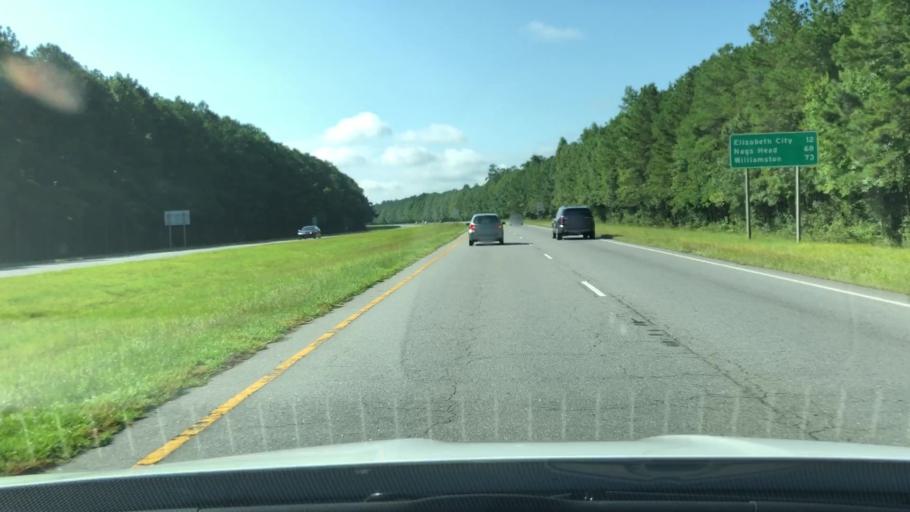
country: US
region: North Carolina
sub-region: Pasquotank County
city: Elizabeth City
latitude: 36.4130
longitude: -76.3406
